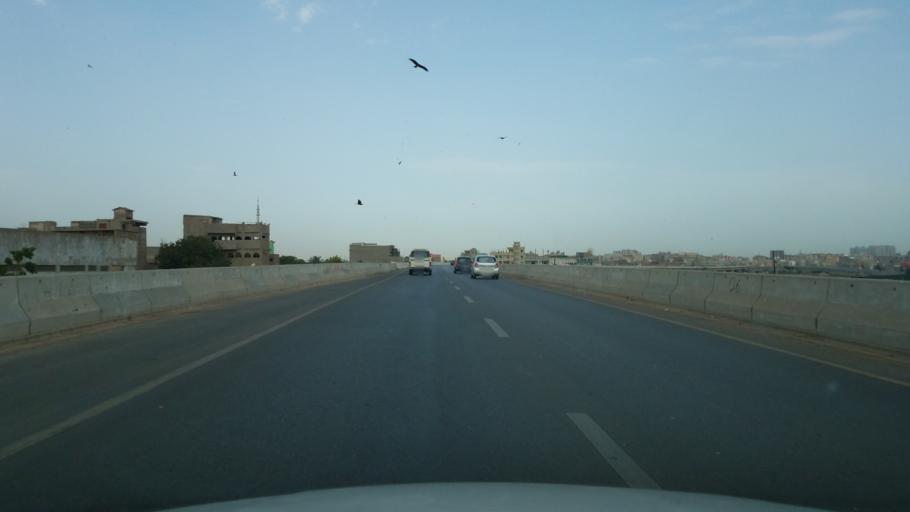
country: PK
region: Sindh
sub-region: Karachi District
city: Karachi
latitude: 24.8823
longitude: 67.0029
